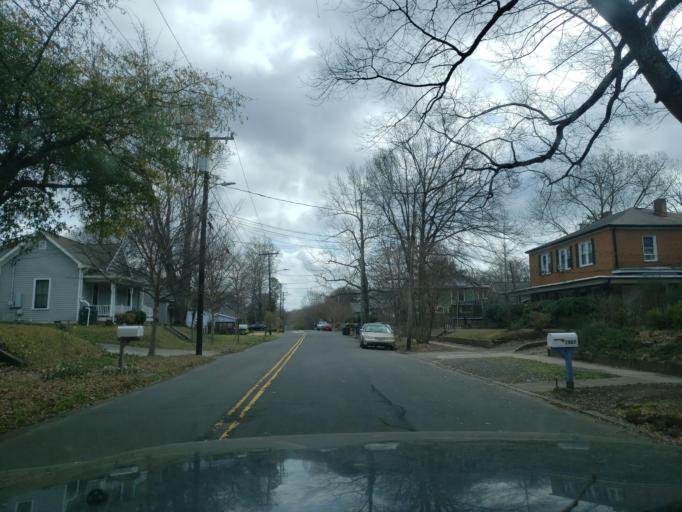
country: US
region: North Carolina
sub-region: Durham County
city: Durham
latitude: 35.9867
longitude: -78.9250
